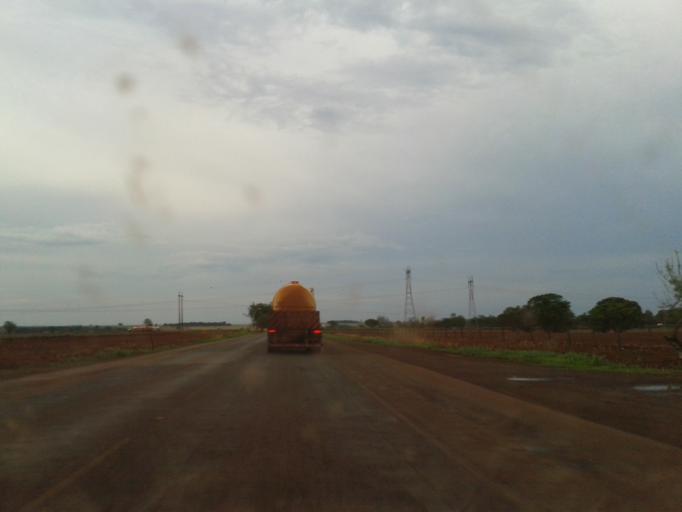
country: BR
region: Goias
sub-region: Santa Helena De Goias
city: Santa Helena de Goias
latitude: -17.9639
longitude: -50.4983
